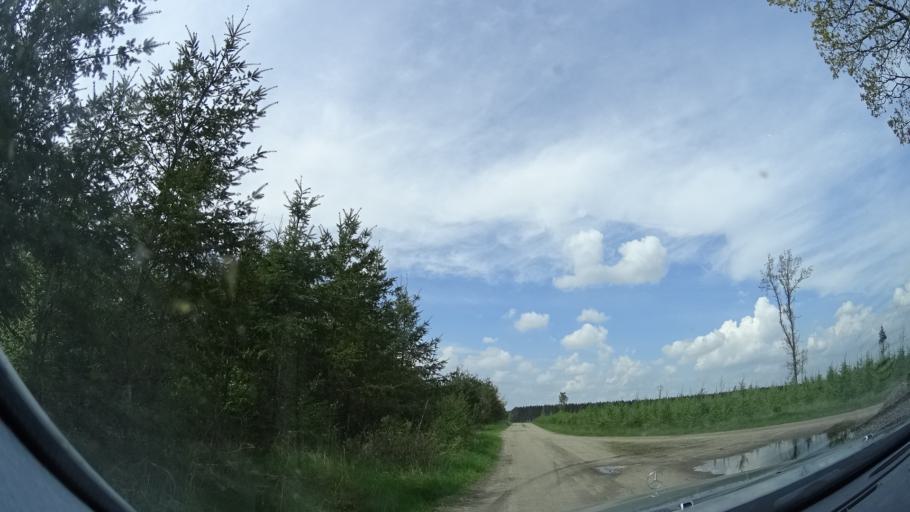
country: SE
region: Skane
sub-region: Sjobo Kommun
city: Sjoebo
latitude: 55.6651
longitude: 13.6582
